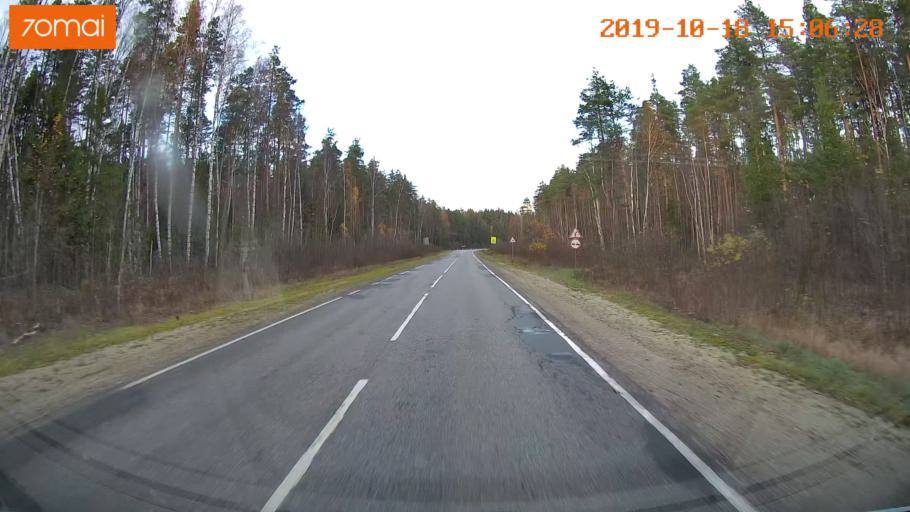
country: RU
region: Vladimir
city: Gus'-Khrustal'nyy
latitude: 55.5307
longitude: 40.5789
